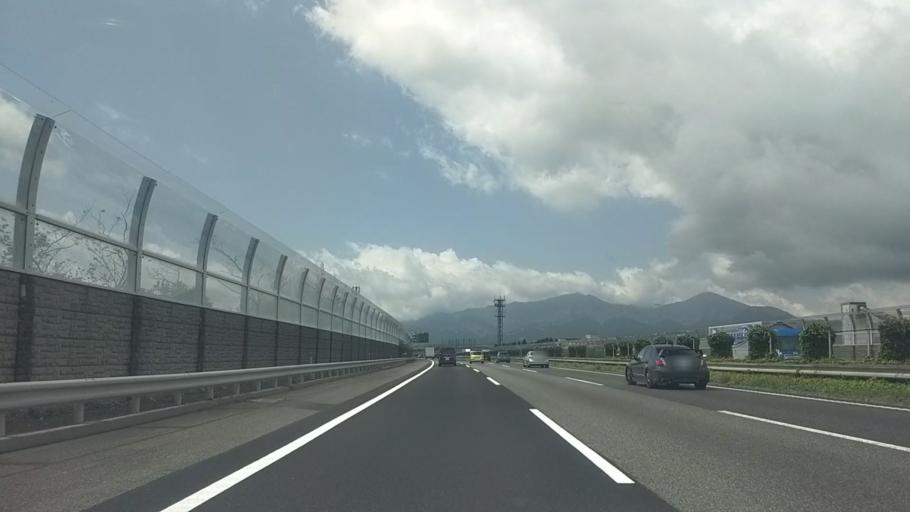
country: JP
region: Shizuoka
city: Gotemba
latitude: 35.2845
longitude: 138.9266
